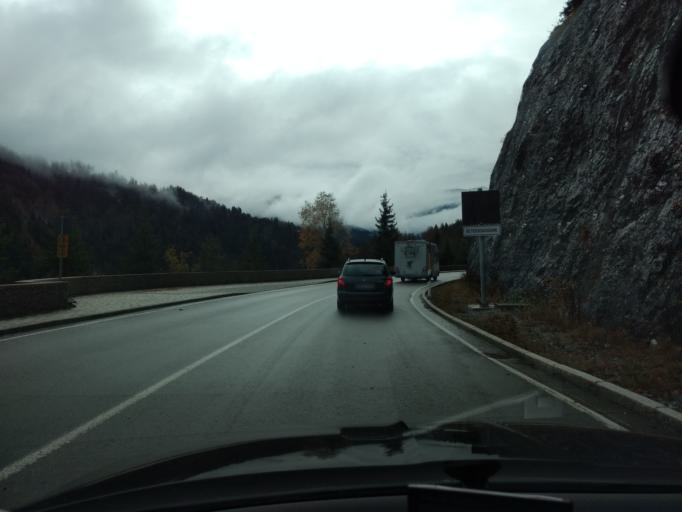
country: DE
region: Bavaria
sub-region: Upper Bavaria
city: Lenggries
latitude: 47.5857
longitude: 11.5485
